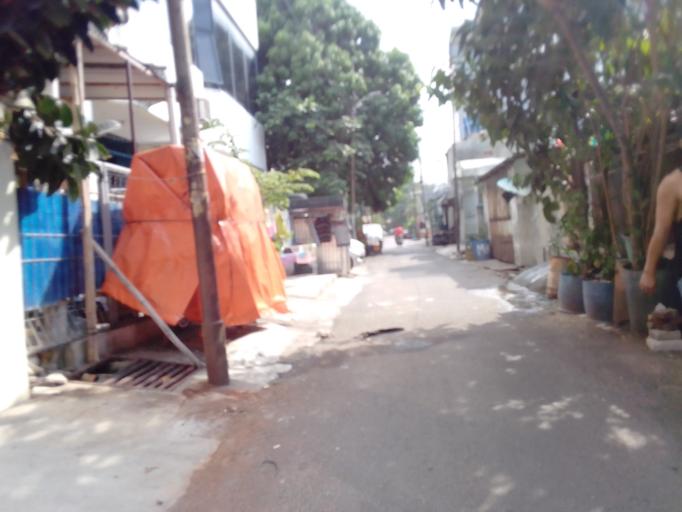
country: ID
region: Jakarta Raya
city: Jakarta
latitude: -6.1619
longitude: 106.8118
